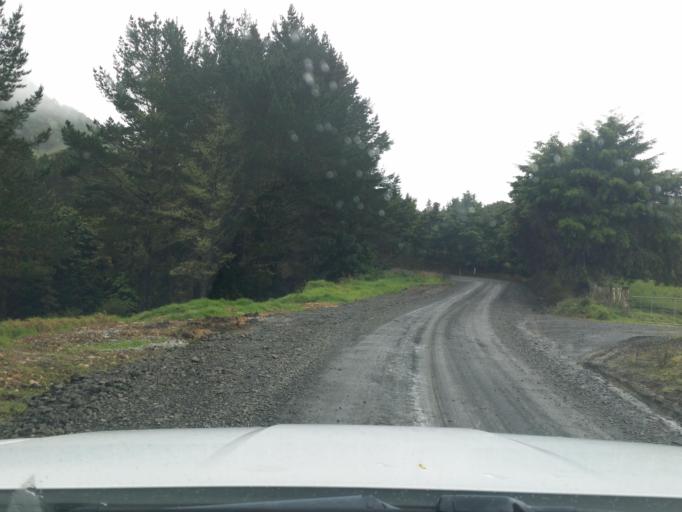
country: NZ
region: Northland
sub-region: Kaipara District
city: Dargaville
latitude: -35.7809
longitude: 173.9887
